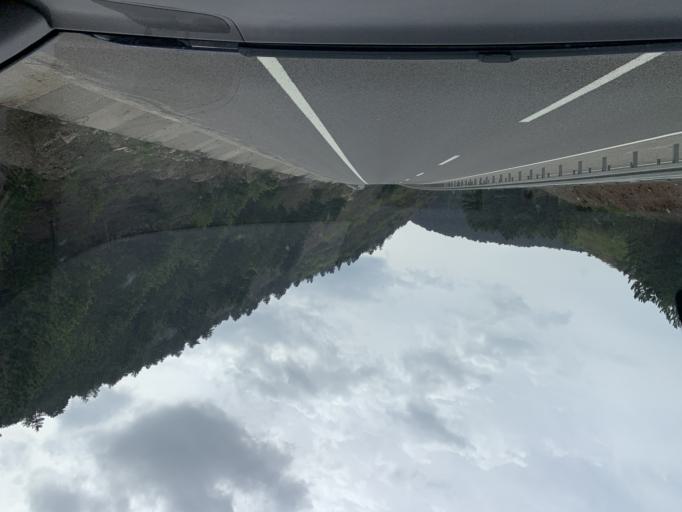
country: TR
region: Bolu
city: Yenicaga
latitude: 40.8268
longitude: 32.0459
